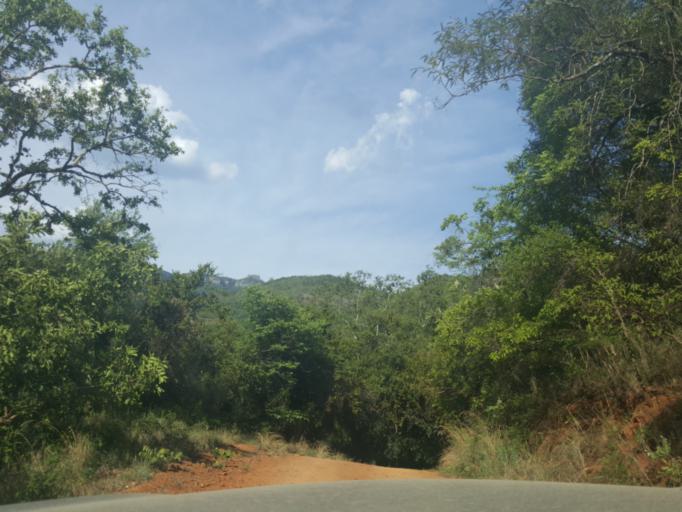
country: ZA
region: Limpopo
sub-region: Mopani District Municipality
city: Hoedspruit
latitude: -24.5939
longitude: 30.8252
